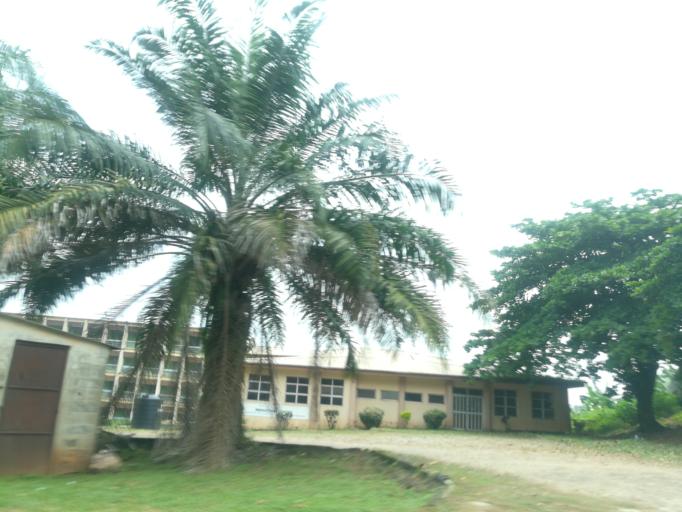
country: NG
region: Oyo
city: Ibadan
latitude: 7.4099
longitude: 3.9073
